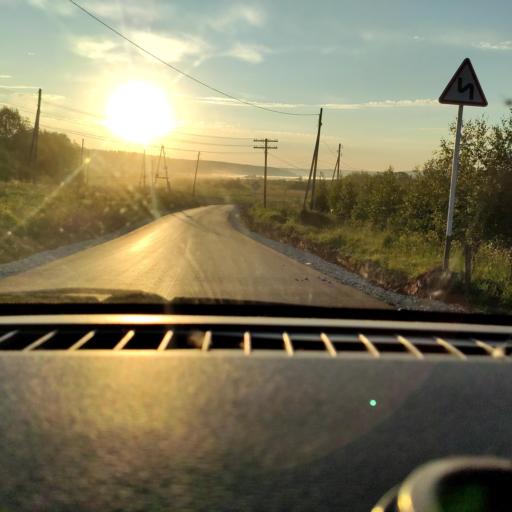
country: RU
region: Perm
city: Sylva
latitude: 57.8384
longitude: 56.6909
